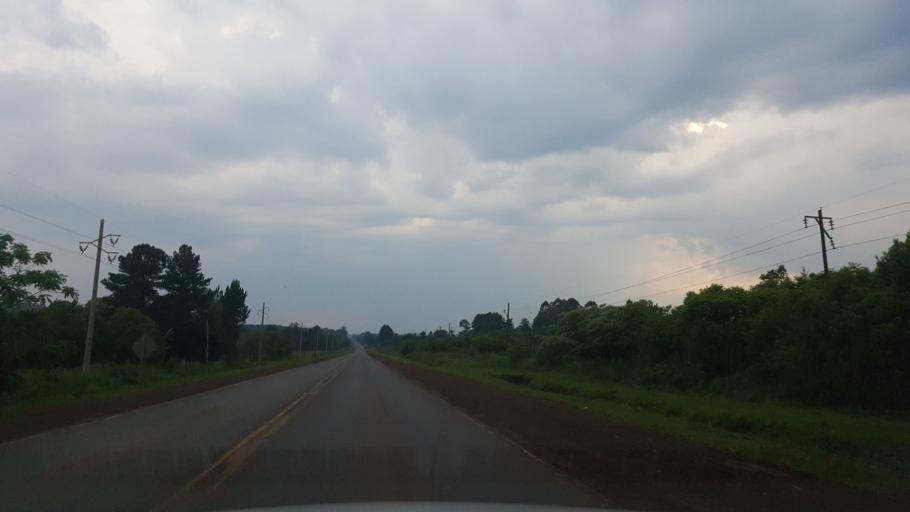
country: AR
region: Misiones
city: Jardin America
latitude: -27.0323
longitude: -55.2210
